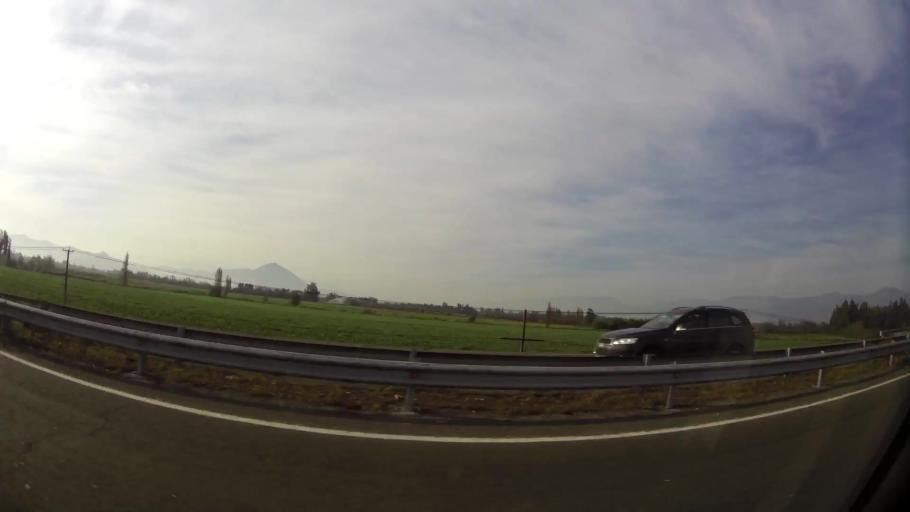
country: CL
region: Santiago Metropolitan
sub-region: Provincia de Talagante
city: Talagante
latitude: -33.6660
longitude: -70.9096
